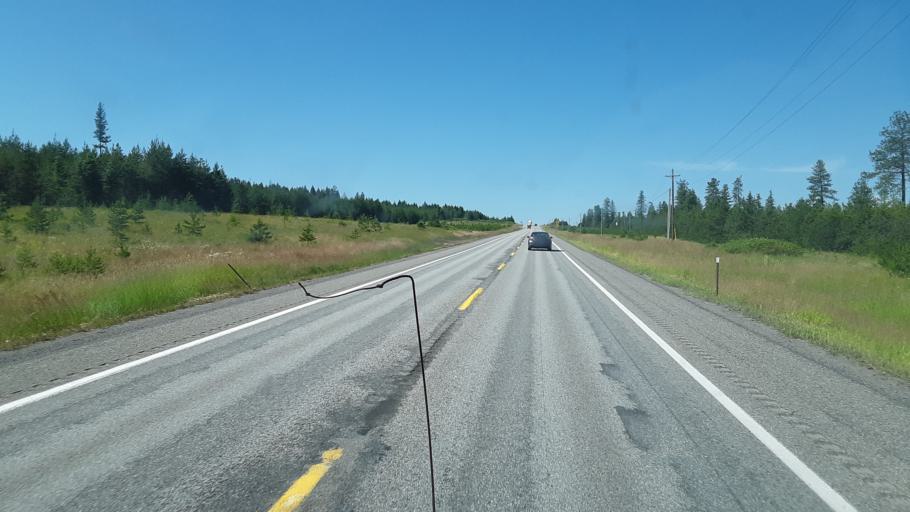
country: US
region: Idaho
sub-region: Kootenai County
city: Spirit Lake
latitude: 48.0133
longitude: -116.6607
